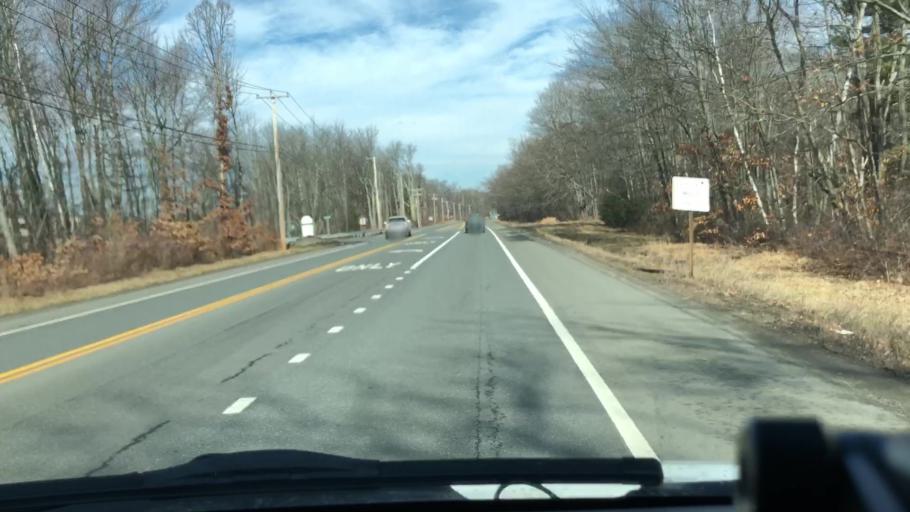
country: US
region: Massachusetts
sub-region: Franklin County
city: South Deerfield
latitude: 42.4937
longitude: -72.6105
